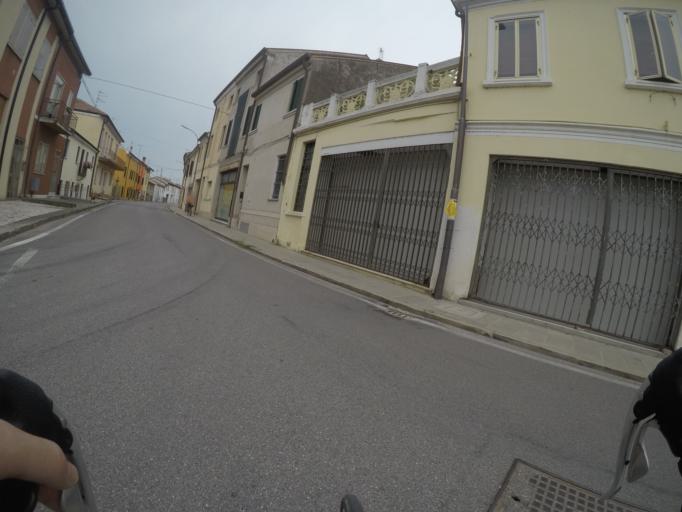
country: IT
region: Veneto
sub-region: Provincia di Rovigo
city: Costa di Rovigo
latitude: 45.0479
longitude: 11.6932
